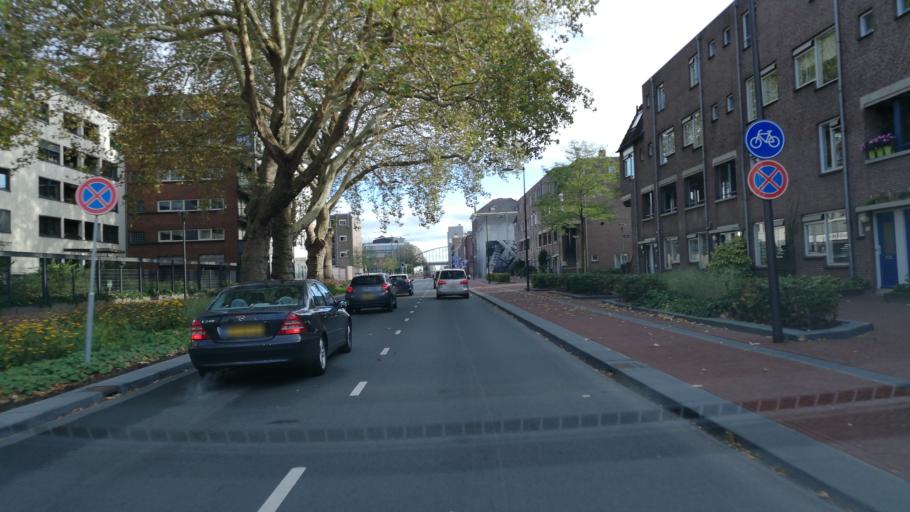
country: NL
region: Gelderland
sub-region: Gemeente Arnhem
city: Arnhem
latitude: 51.9797
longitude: 5.9044
